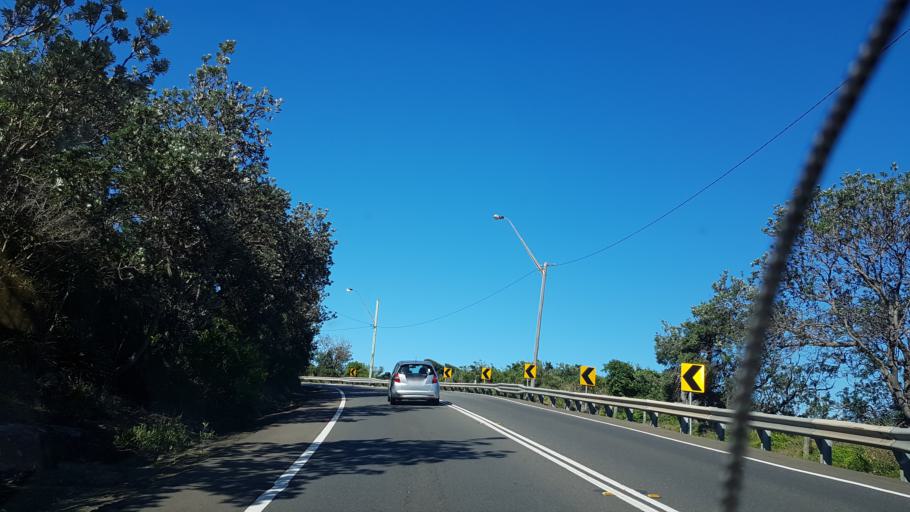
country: AU
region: New South Wales
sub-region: Pittwater
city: Bilgola Beach
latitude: -33.6486
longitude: 151.3264
